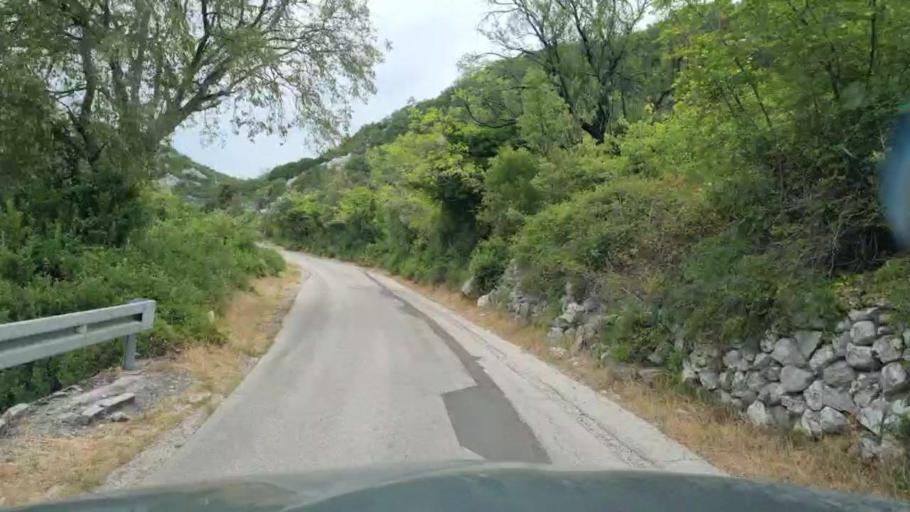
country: BA
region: Federation of Bosnia and Herzegovina
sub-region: Hercegovacko-Bosanski Kanton
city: Neum
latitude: 42.9185
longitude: 17.6714
